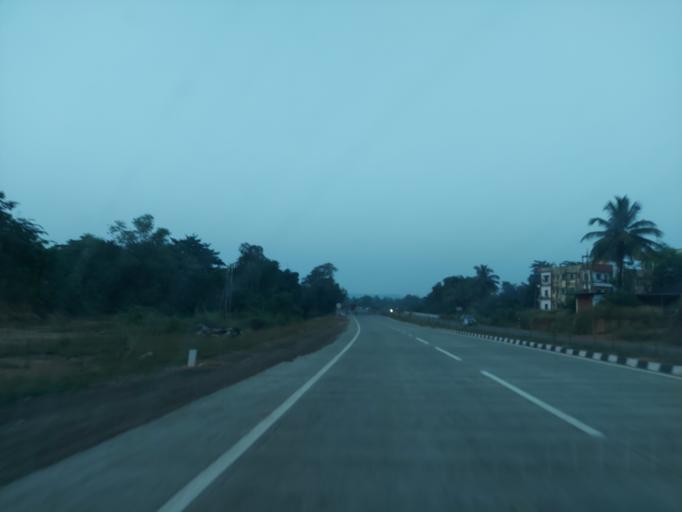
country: IN
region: Maharashtra
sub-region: Sindhudurg
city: Kudal
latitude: 16.0962
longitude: 73.7064
